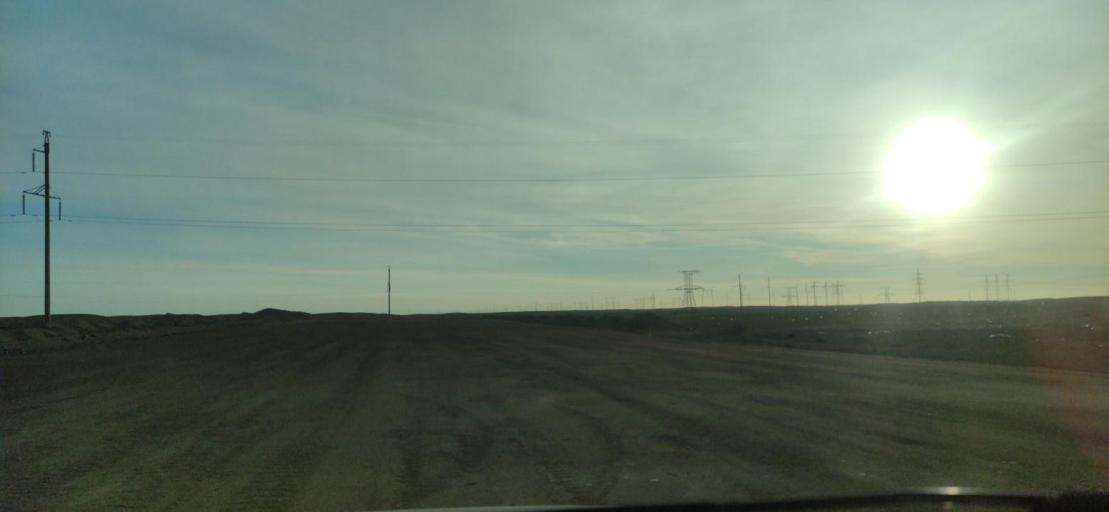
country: KZ
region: Qaraghandy
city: Saryshaghan
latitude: 46.1235
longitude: 73.5957
